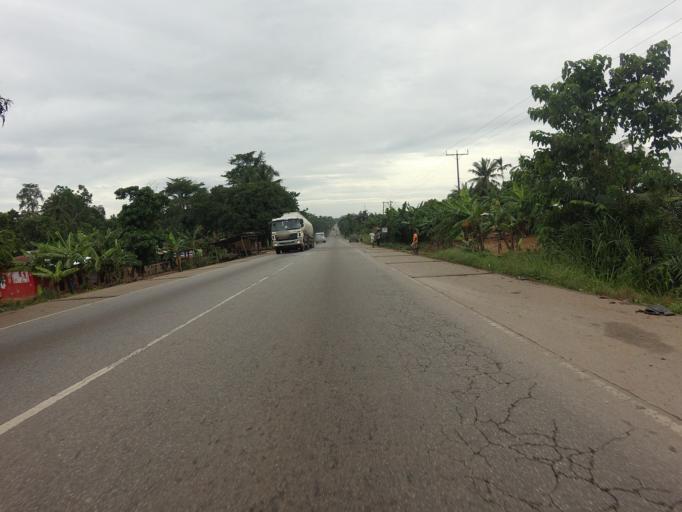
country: GH
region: Eastern
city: Nkawkaw
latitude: 6.4918
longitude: -0.6818
